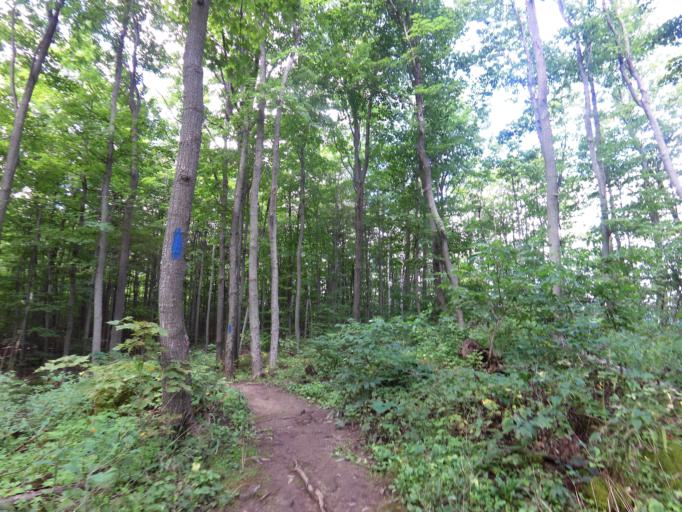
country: CA
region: Ontario
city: Owen Sound
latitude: 44.9546
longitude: -81.1429
